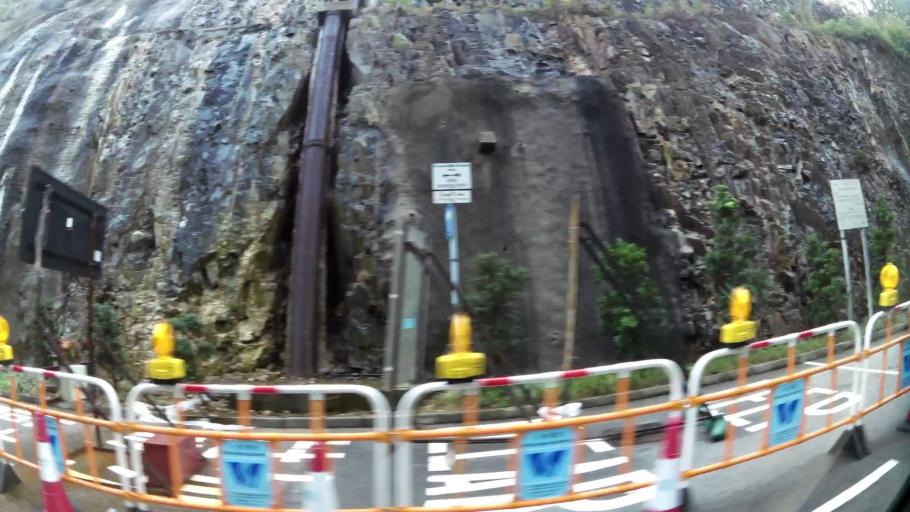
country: HK
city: Sok Kwu Wan
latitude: 22.2394
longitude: 114.1537
